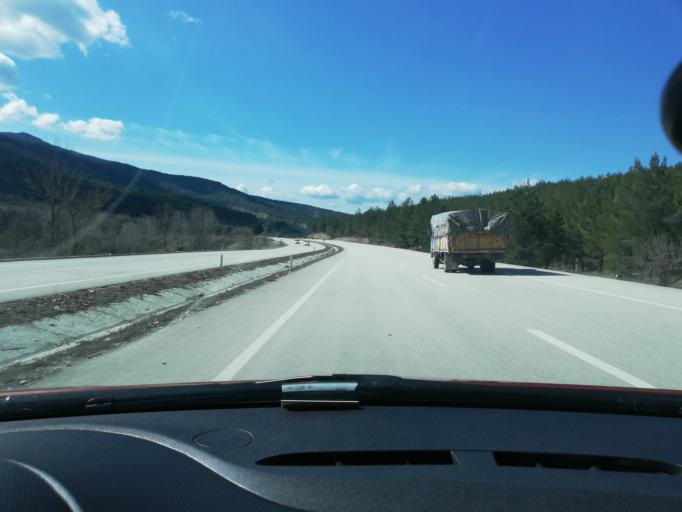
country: TR
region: Karabuk
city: Safranbolu
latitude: 41.2011
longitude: 32.8207
